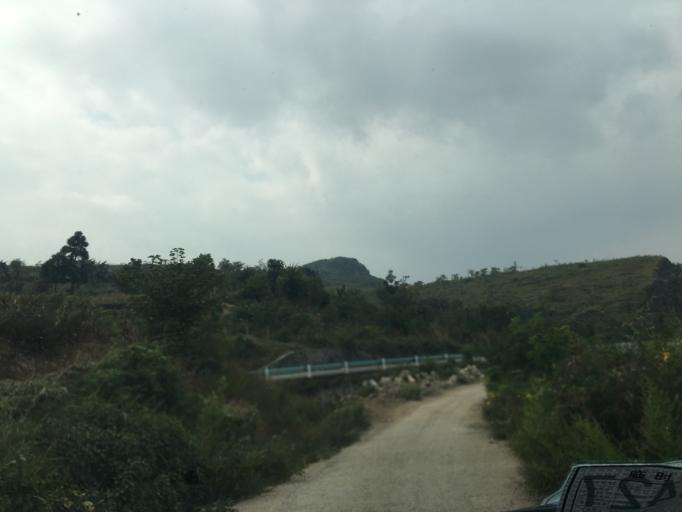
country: CN
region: Guangxi Zhuangzu Zizhiqu
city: Xinzhou
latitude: 25.5693
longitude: 105.6166
